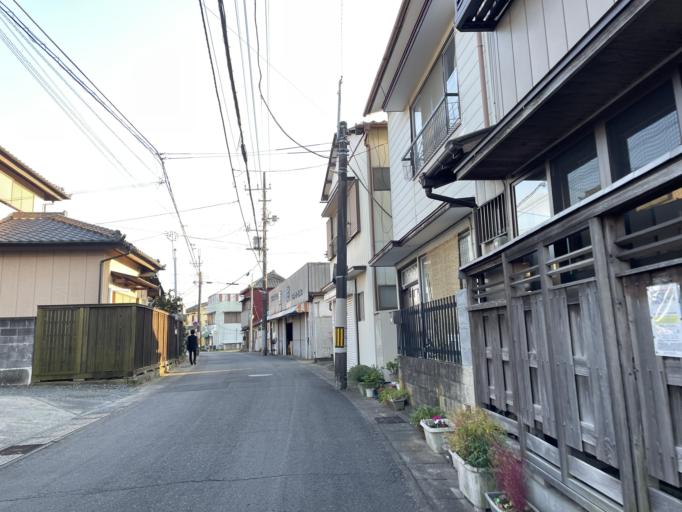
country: JP
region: Ibaraki
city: Ishioka
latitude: 36.1879
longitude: 140.2773
